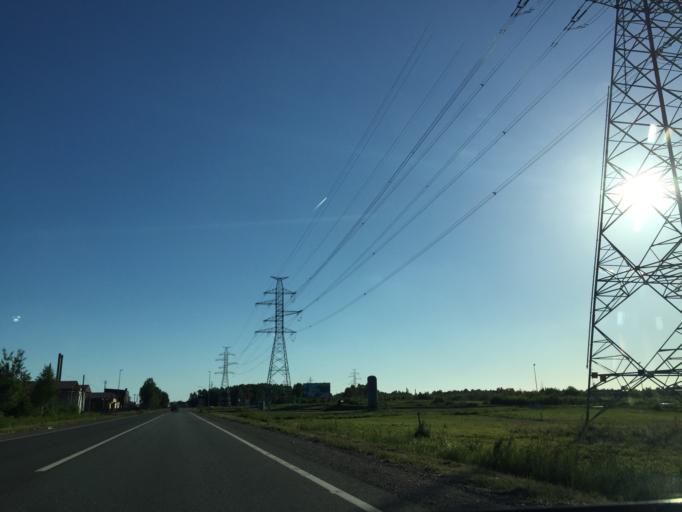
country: LV
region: Ventspils
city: Ventspils
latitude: 57.3983
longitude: 21.6522
